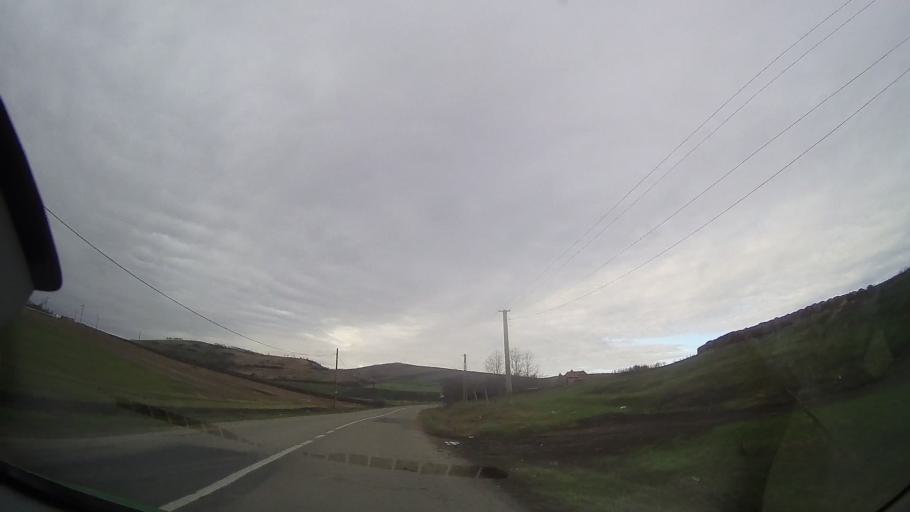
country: RO
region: Cluj
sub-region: Comuna Camarasu
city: Camarasu
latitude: 46.8033
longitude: 24.1493
